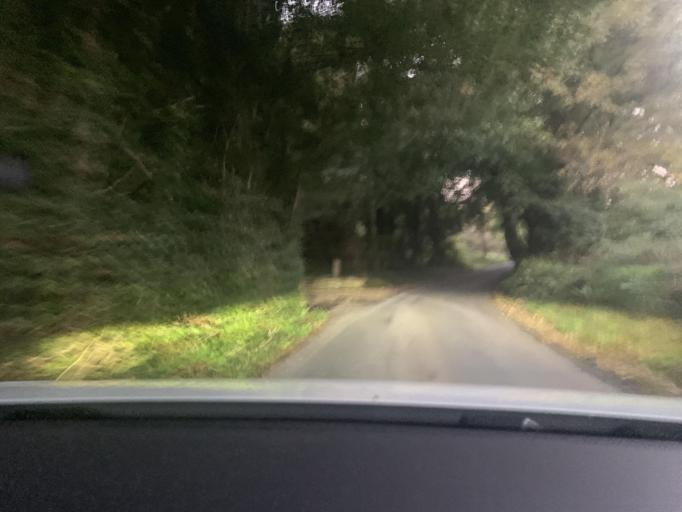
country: IE
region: Connaught
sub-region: County Leitrim
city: Manorhamilton
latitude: 54.2575
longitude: -8.3043
